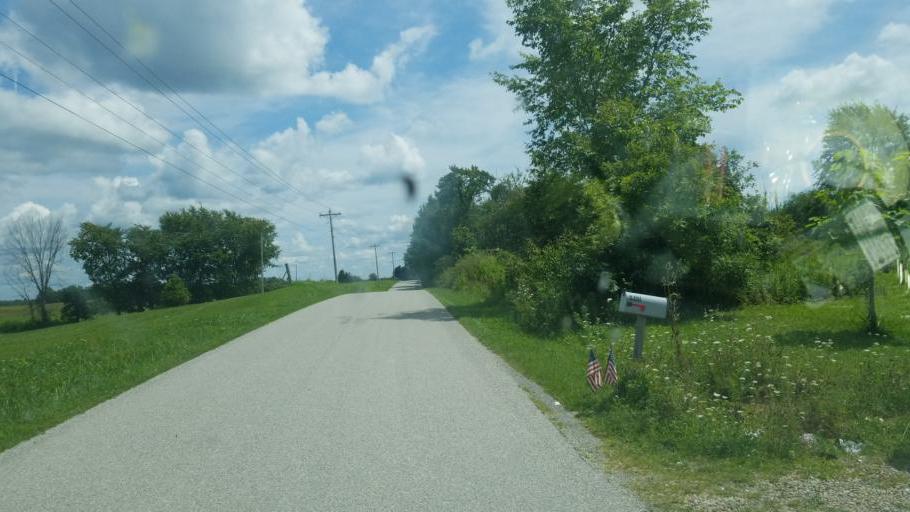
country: US
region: Ohio
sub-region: Knox County
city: Centerburg
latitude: 40.3750
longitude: -82.7163
